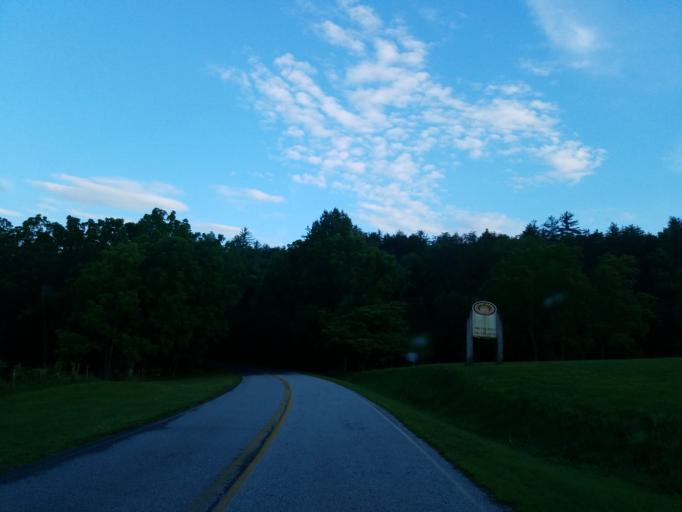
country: US
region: Georgia
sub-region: Fannin County
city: Blue Ridge
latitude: 34.7104
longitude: -84.2355
